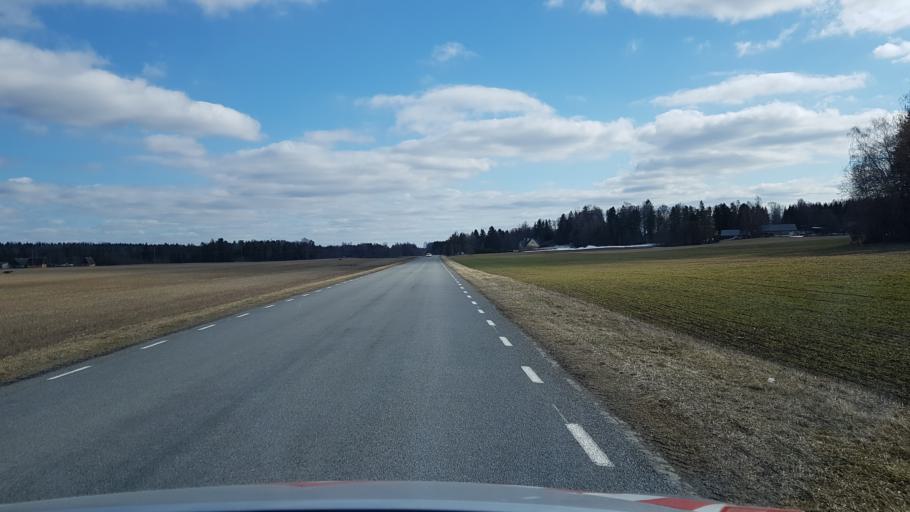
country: EE
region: Laeaene-Virumaa
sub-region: Tamsalu vald
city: Tamsalu
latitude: 59.1741
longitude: 26.0553
